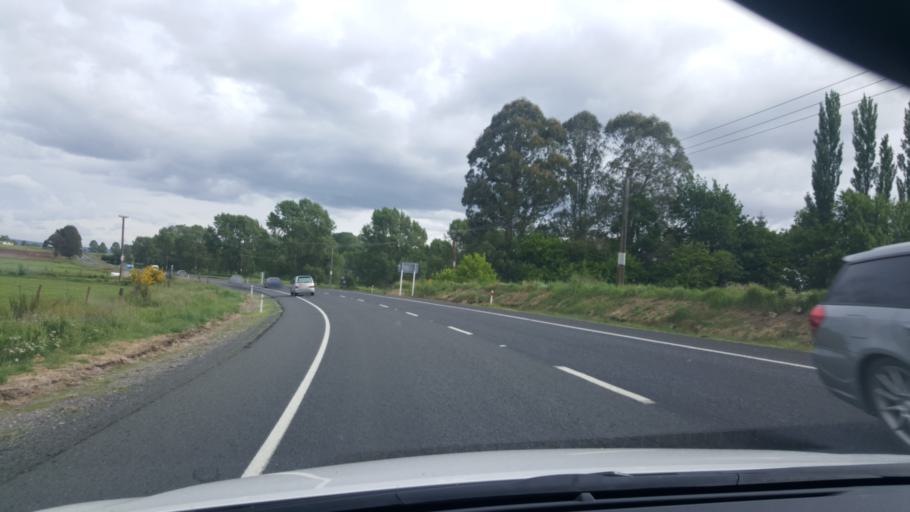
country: NZ
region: Waikato
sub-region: Taupo District
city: Taupo
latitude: -38.4869
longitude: 176.2904
